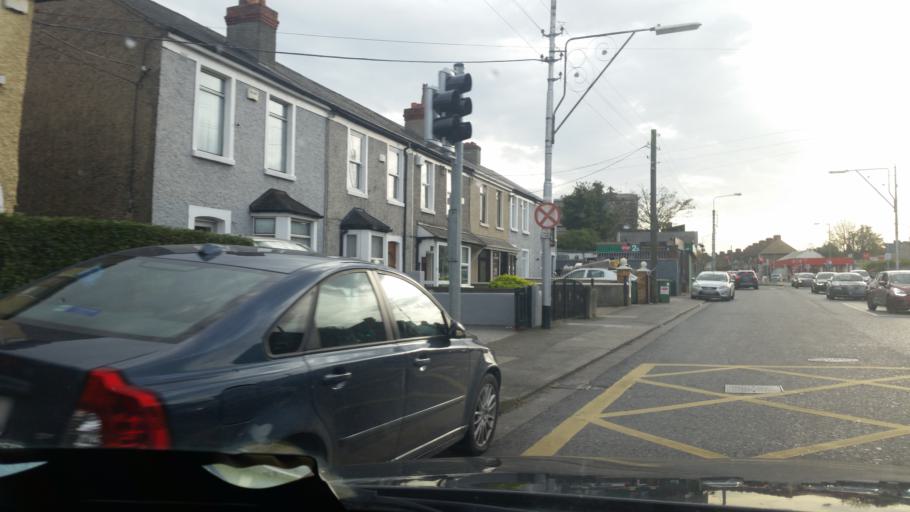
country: IE
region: Leinster
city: Rialto
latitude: 53.3312
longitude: -6.2979
